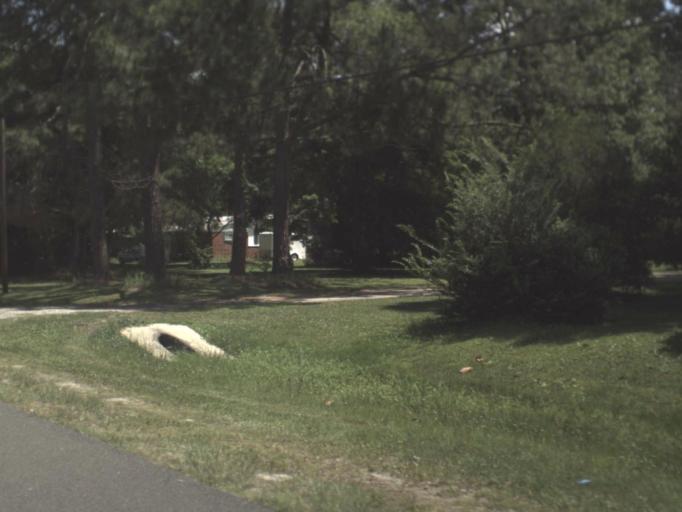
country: US
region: Florida
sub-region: Nassau County
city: Nassau Village-Ratliff
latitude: 30.5381
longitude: -81.7756
